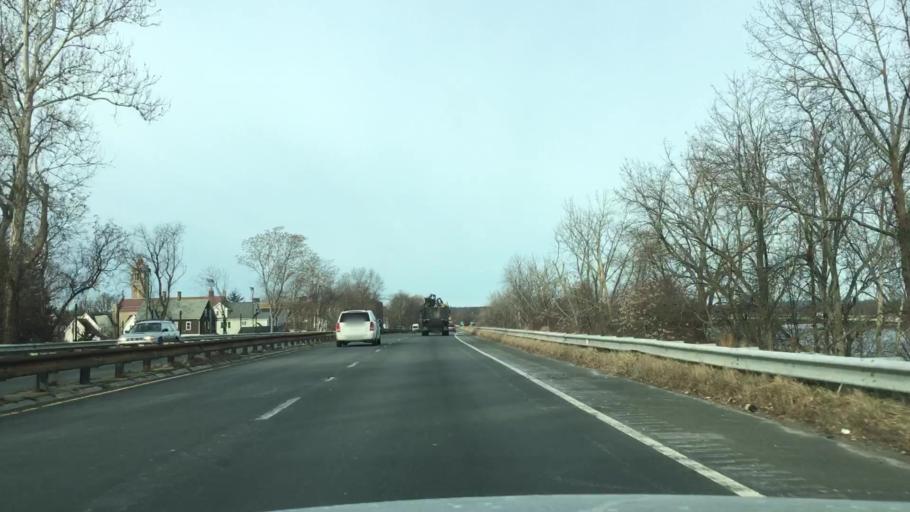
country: US
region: Massachusetts
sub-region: Hampden County
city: West Springfield
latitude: 42.1020
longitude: -72.6055
